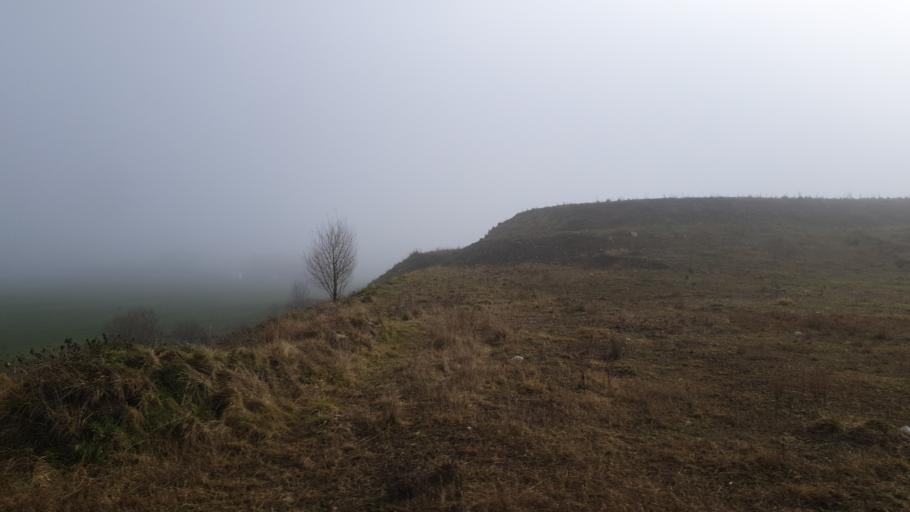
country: CH
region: Fribourg
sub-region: Veveyse District
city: Chatel-Saint-Denis
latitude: 46.5524
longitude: 6.9046
